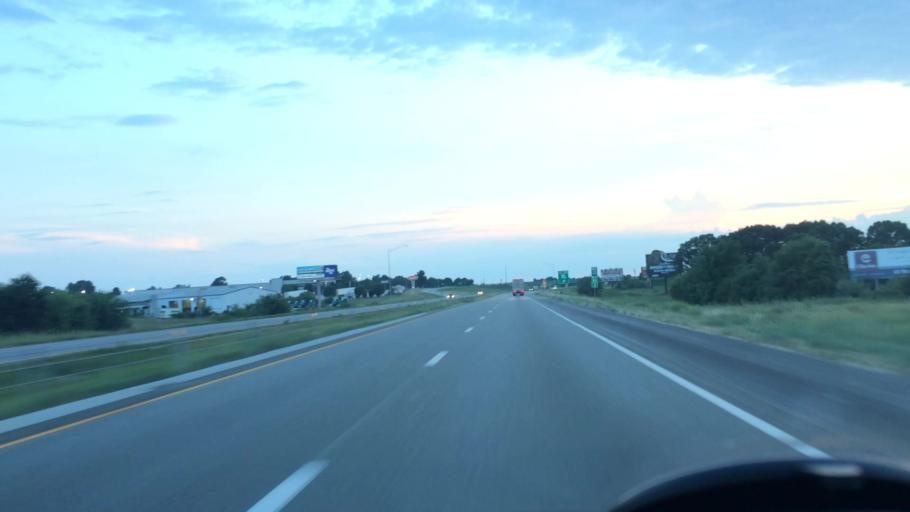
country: US
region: Missouri
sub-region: Greene County
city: Strafford
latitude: 37.2529
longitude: -93.1757
